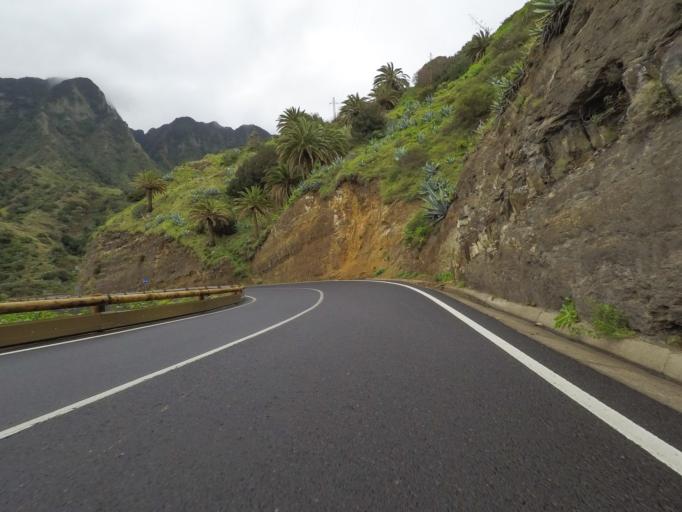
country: ES
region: Canary Islands
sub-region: Provincia de Santa Cruz de Tenerife
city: Hermigua
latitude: 28.1432
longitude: -17.1968
